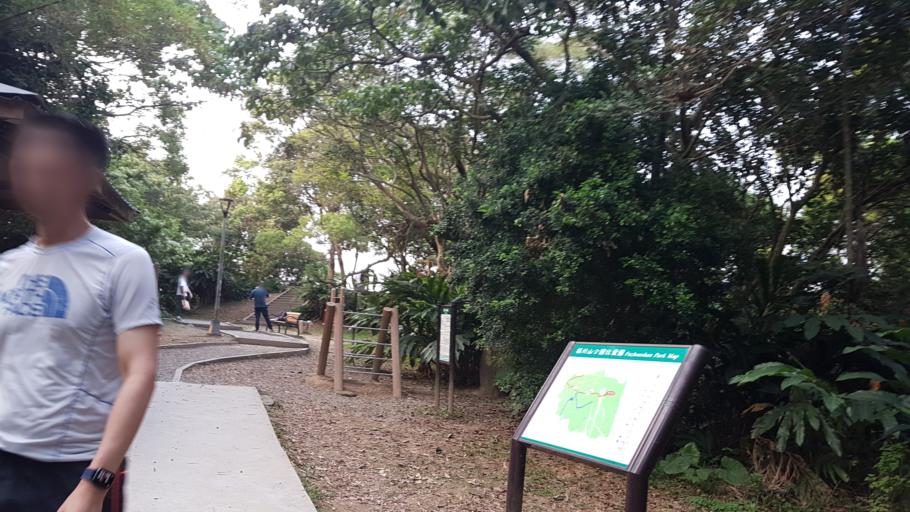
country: TW
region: Taipei
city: Taipei
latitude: 25.0166
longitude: 121.5548
